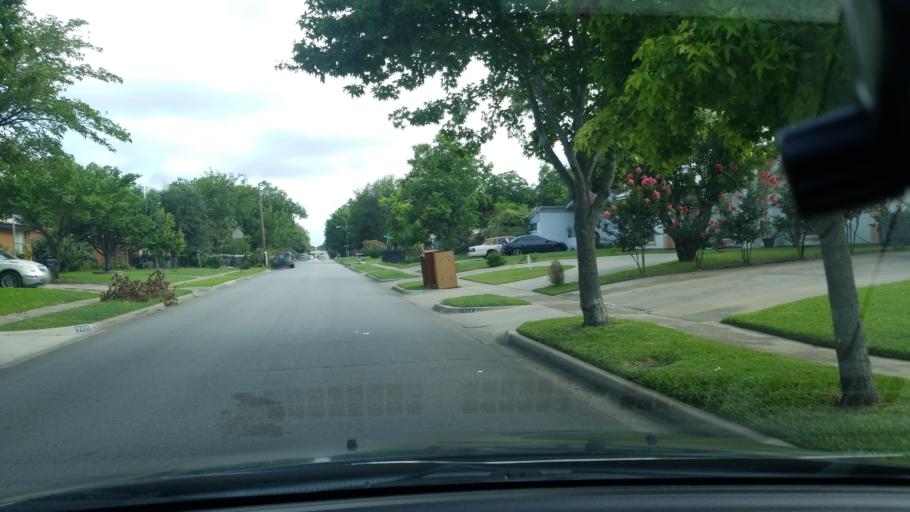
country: US
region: Texas
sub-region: Dallas County
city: Mesquite
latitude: 32.8176
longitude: -96.6776
